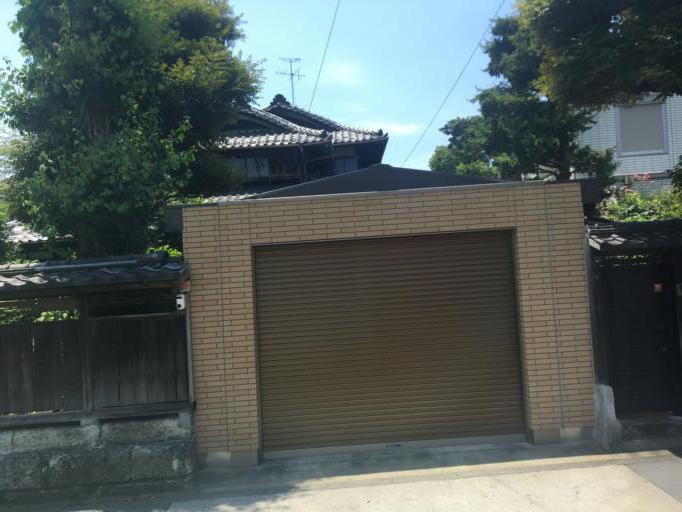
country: JP
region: Saitama
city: Kawaguchi
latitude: 35.7617
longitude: 139.6901
